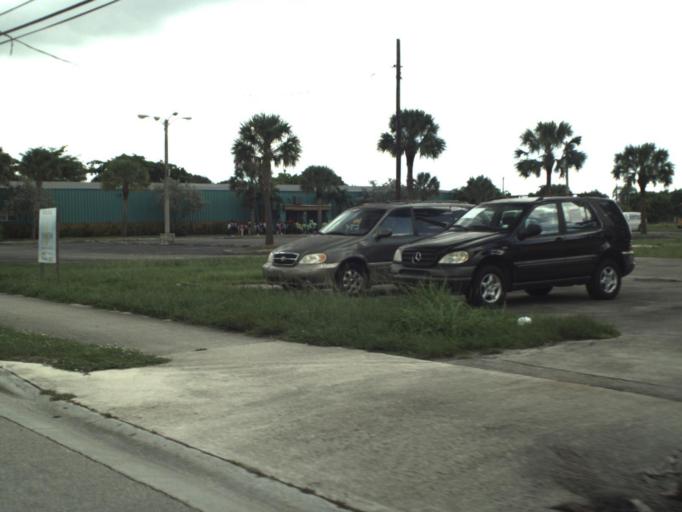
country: US
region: Florida
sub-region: Palm Beach County
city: Greenacres City
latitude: 26.6293
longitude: -80.1460
